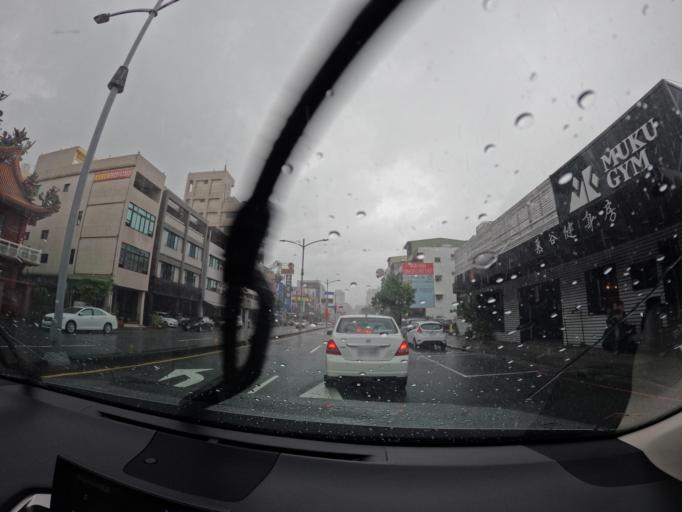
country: TW
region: Kaohsiung
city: Kaohsiung
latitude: 22.6685
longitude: 120.3108
